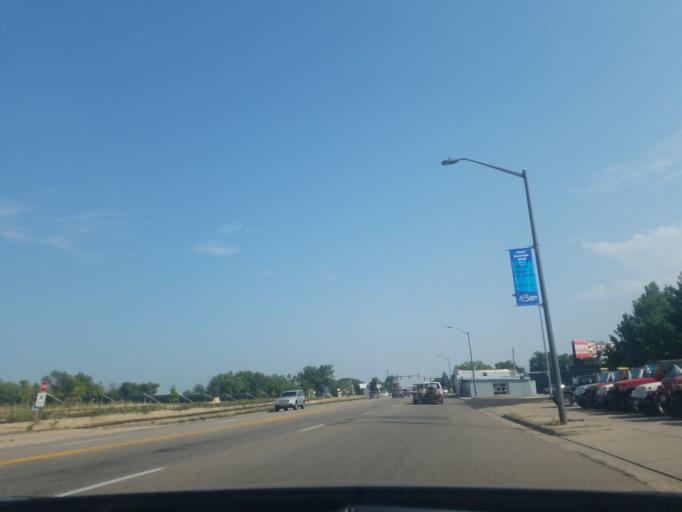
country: US
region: Colorado
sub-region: Larimer County
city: Fort Collins
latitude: 40.5828
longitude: -105.0653
